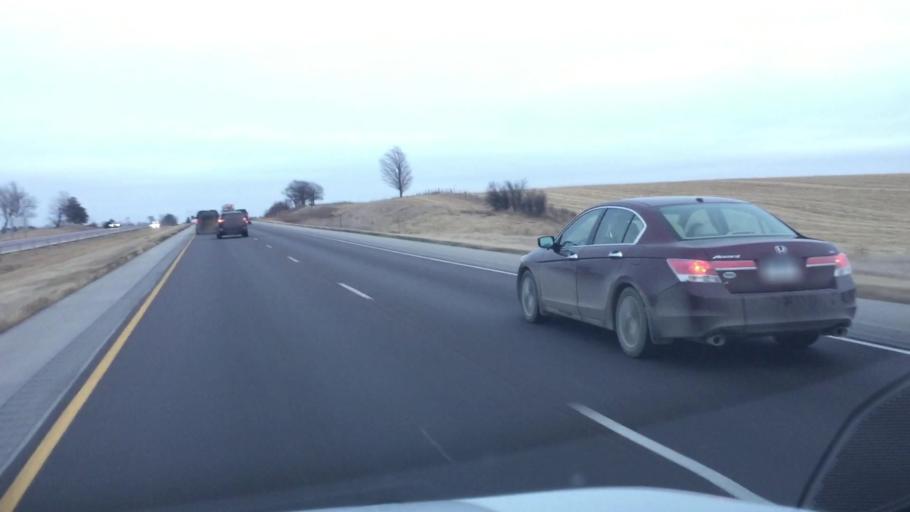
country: US
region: Iowa
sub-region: Poweshiek County
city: Grinnell
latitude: 41.6952
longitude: -92.6991
